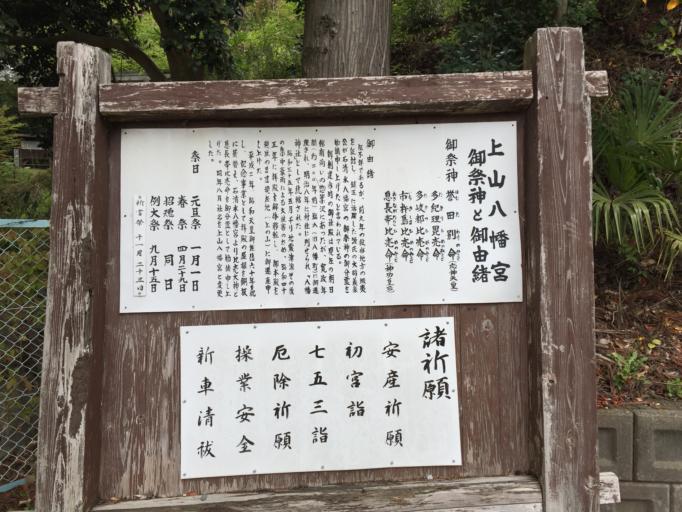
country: JP
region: Miyagi
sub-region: Oshika Gun
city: Onagawa Cho
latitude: 38.6795
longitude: 141.4495
